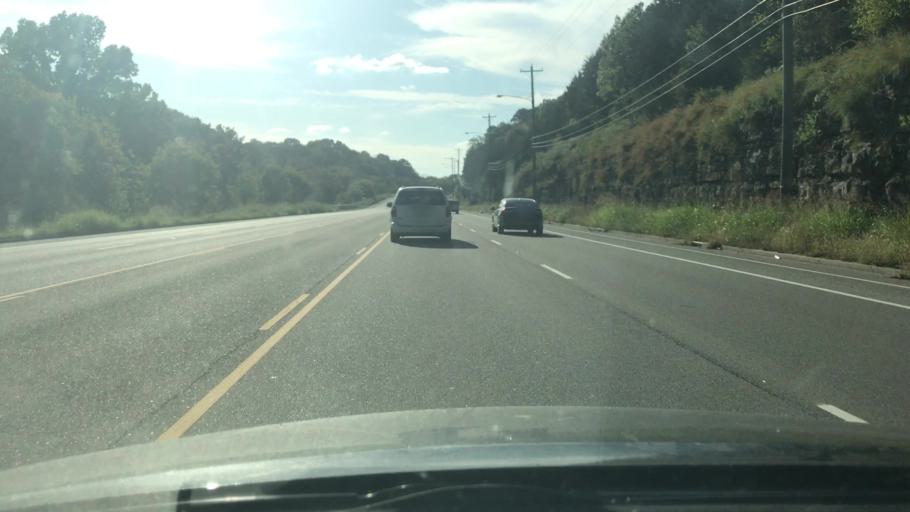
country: US
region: Tennessee
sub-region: Davidson County
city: Belle Meade
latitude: 36.2112
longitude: -86.8996
